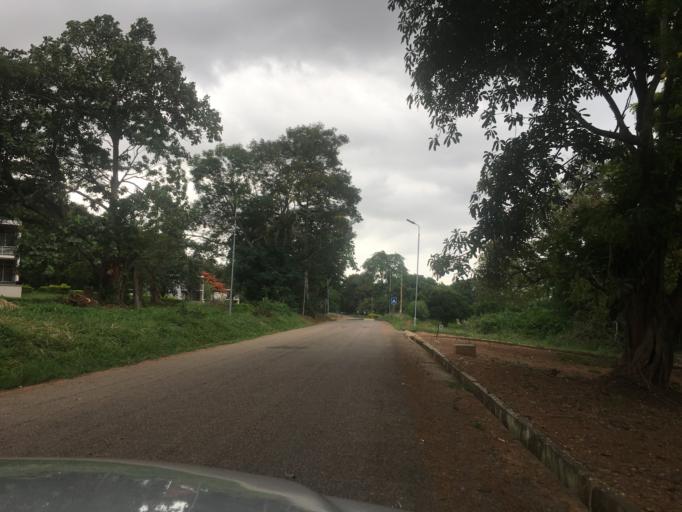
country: GH
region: Ashanti
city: Kumasi
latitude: 6.6751
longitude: -1.5833
